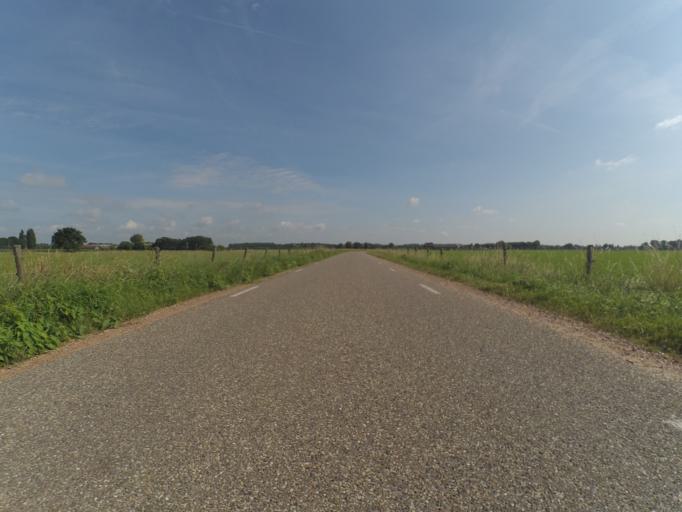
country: NL
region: Utrecht
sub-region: Gemeente Utrechtse Heuvelrug
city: Driebergen-Rijsenburg
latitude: 51.9985
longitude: 5.2767
